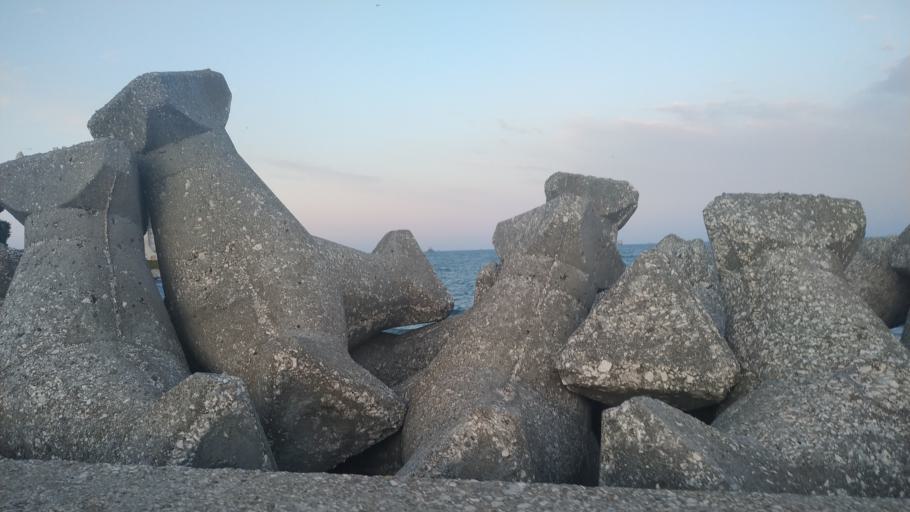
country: RO
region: Constanta
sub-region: Municipiul Constanta
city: Constanta
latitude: 44.1693
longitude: 28.6603
